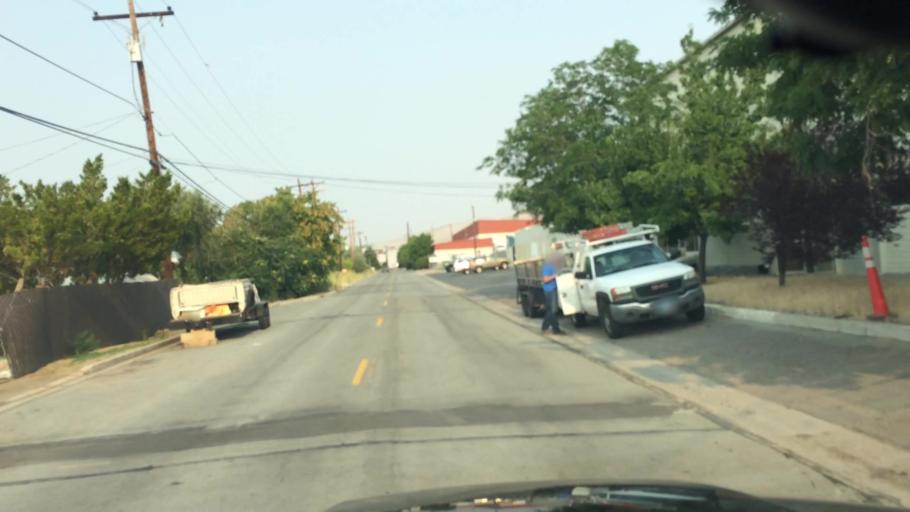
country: US
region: Nevada
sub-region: Washoe County
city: Reno
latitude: 39.5493
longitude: -119.8041
